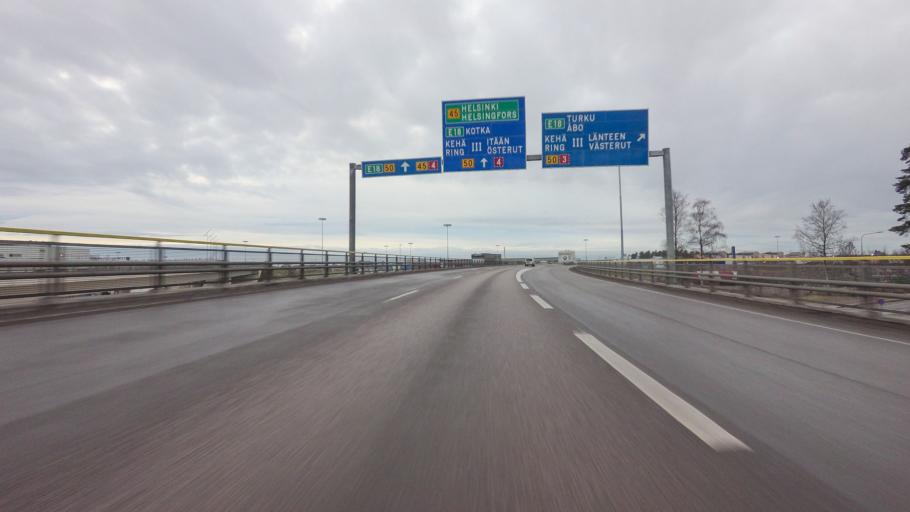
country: FI
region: Uusimaa
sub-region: Helsinki
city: Vantaa
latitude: 60.2979
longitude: 24.9585
